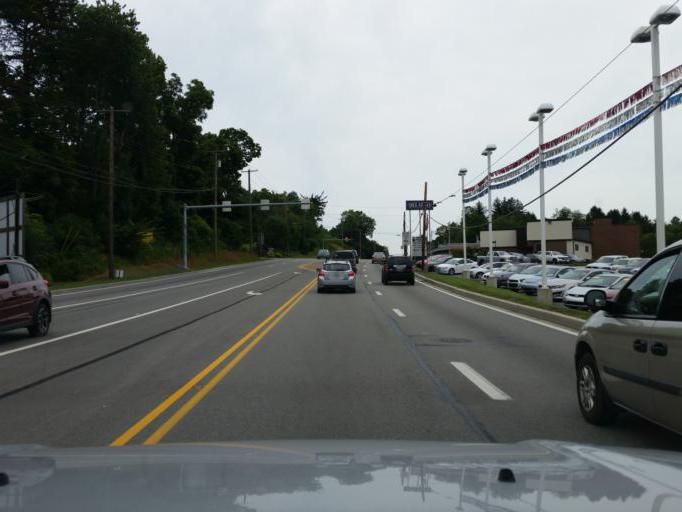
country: US
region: Pennsylvania
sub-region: Westmoreland County
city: Jeannette
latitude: 40.3108
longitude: -79.6097
